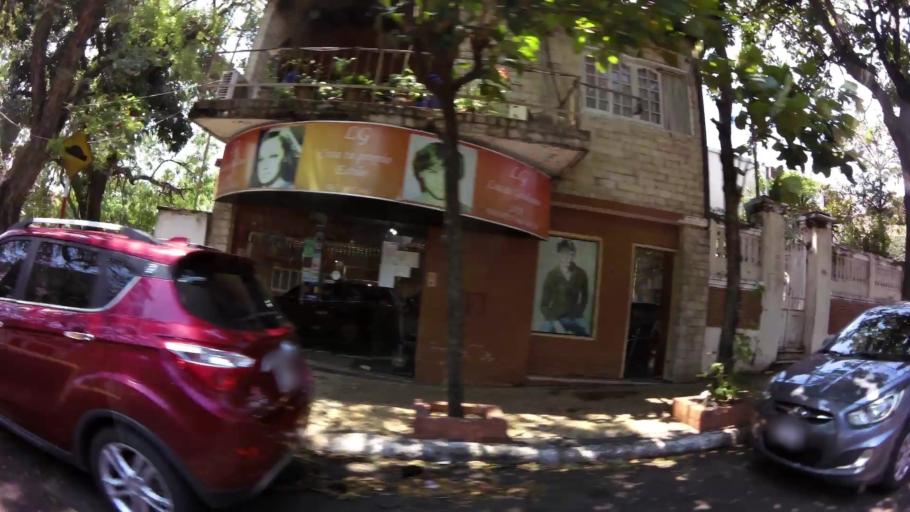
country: PY
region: Asuncion
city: Asuncion
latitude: -25.2909
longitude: -57.6412
